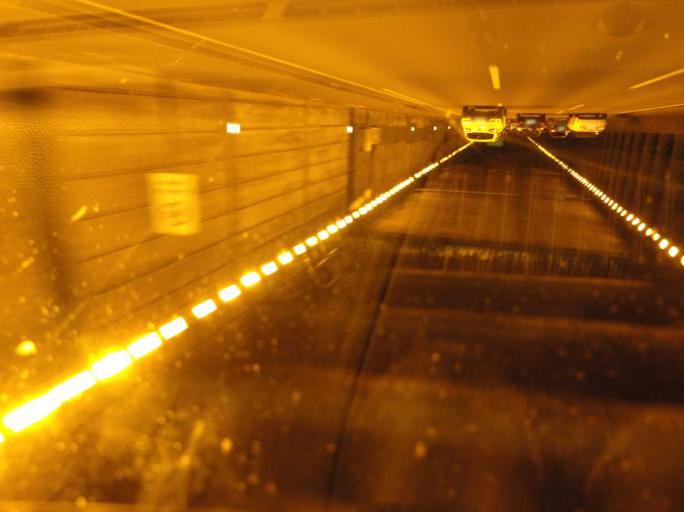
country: ES
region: Catalonia
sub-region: Provincia de Barcelona
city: Nou Barris
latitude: 41.4446
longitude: 2.1744
